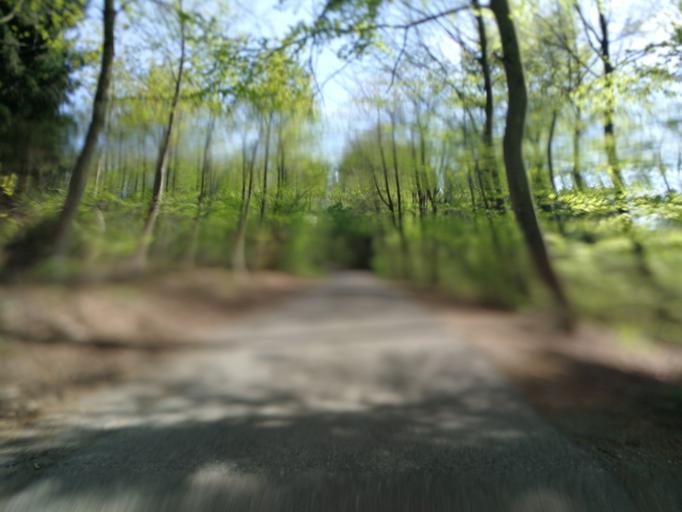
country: CH
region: Zurich
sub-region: Bezirk Hinwil
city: Hinwil
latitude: 47.3023
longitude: 8.8180
